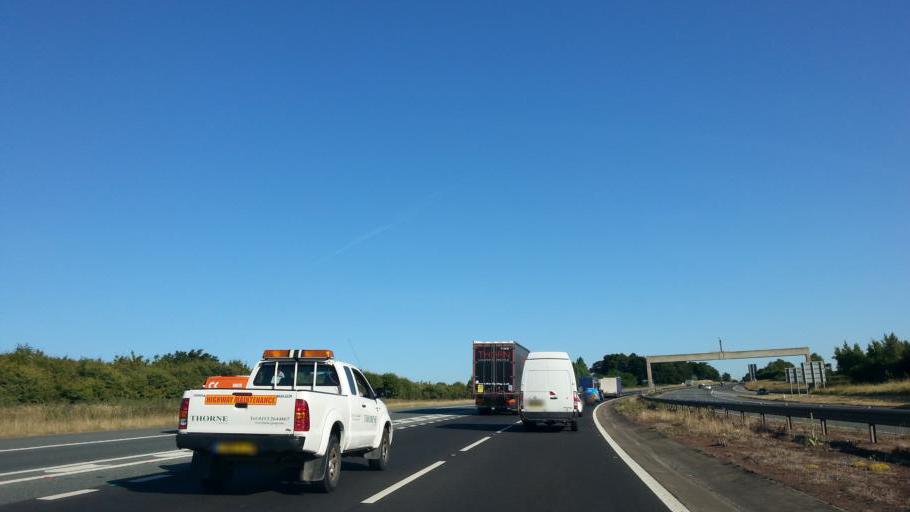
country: GB
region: England
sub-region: City and Borough of Wakefield
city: Darrington
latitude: 53.6832
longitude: -1.2642
